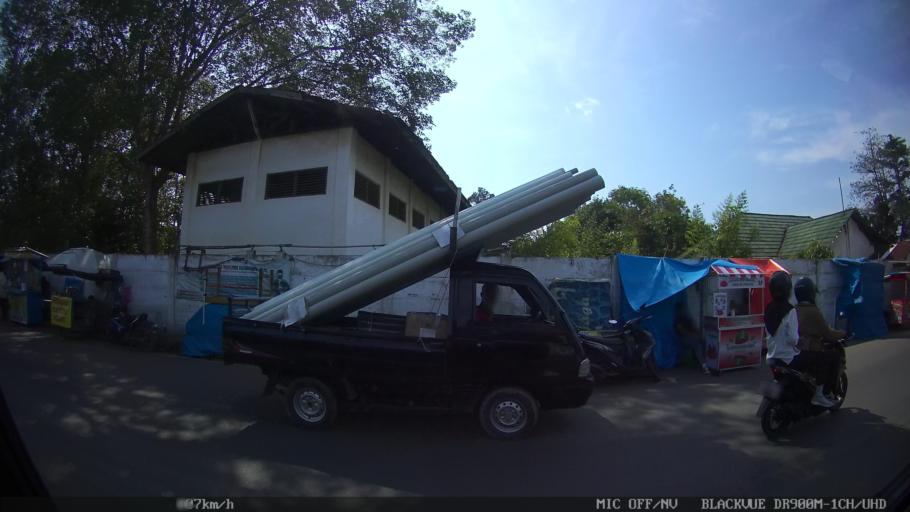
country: ID
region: Lampung
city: Kedaton
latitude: -5.3567
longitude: 105.2370
